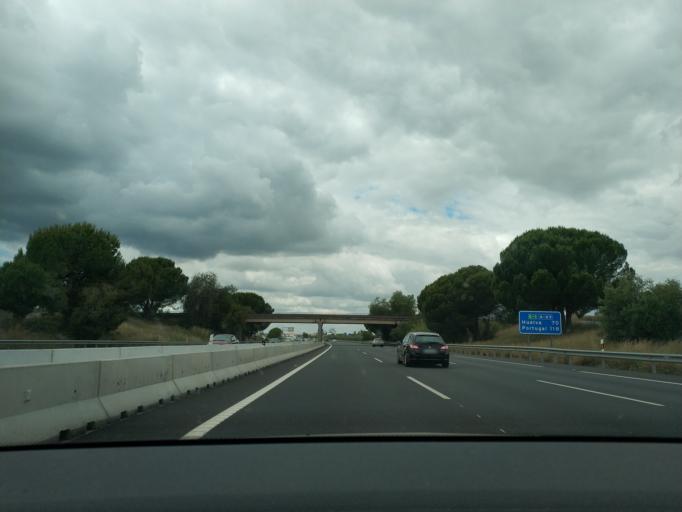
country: ES
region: Andalusia
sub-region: Provincia de Sevilla
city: Benacazon
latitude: 37.3576
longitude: -6.1793
